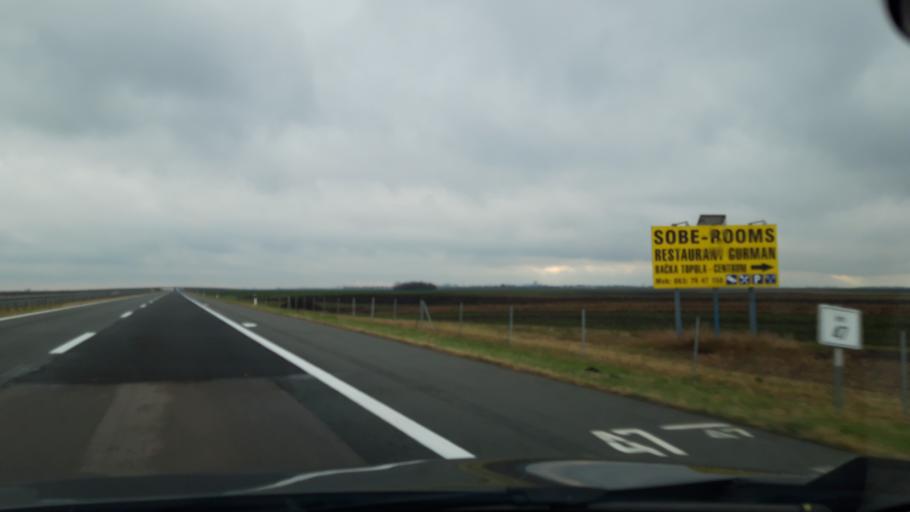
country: RS
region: Autonomna Pokrajina Vojvodina
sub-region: Severnobacki Okrug
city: Backa Topola
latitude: 45.8512
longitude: 19.6956
